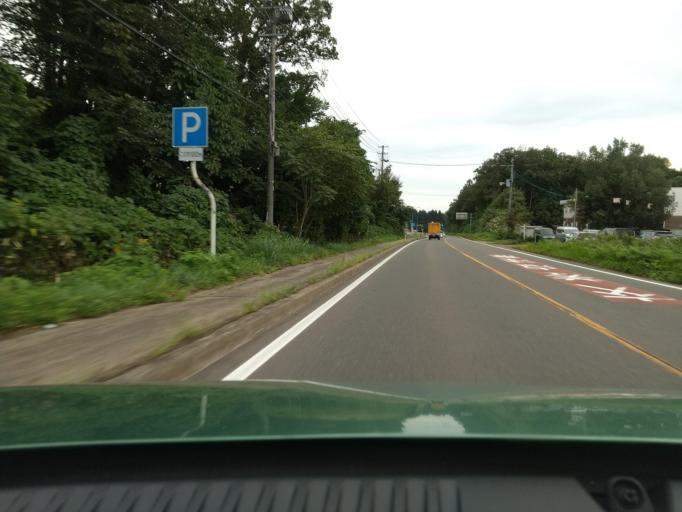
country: JP
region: Akita
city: Yokotemachi
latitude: 39.3453
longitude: 140.5610
